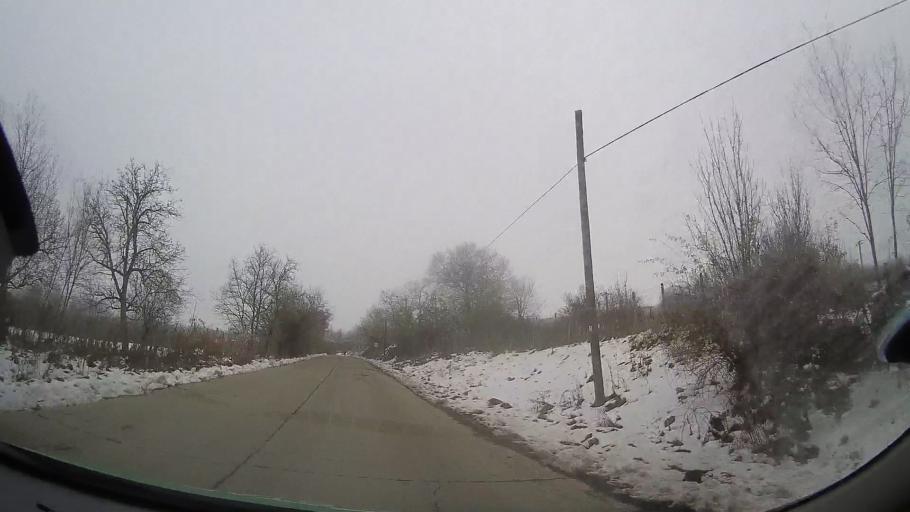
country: RO
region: Vrancea
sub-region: Comuna Boghesti
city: Boghesti
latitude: 46.2052
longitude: 27.4411
